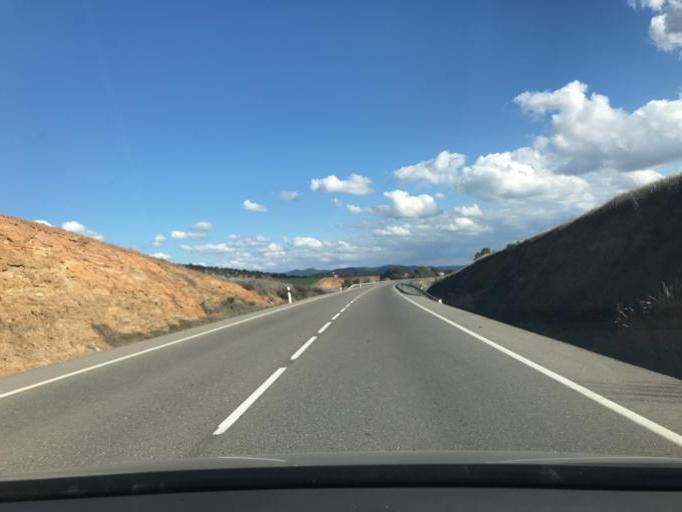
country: ES
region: Andalusia
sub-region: Province of Cordoba
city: Penarroya-Pueblonuevo
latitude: 38.2962
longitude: -5.2410
